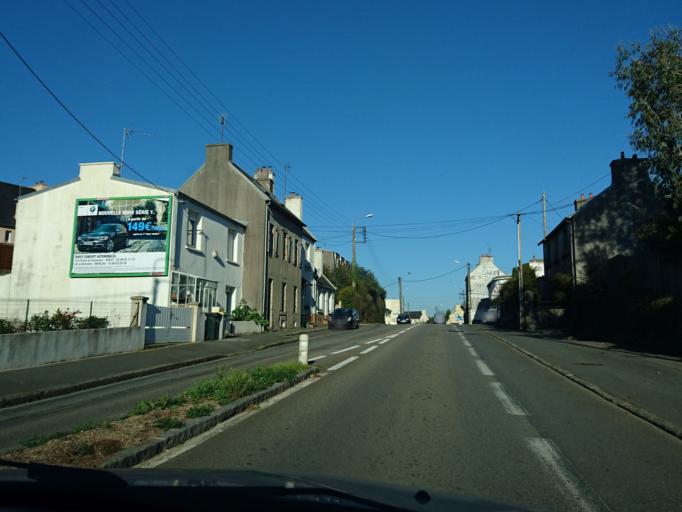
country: FR
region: Brittany
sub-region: Departement du Finistere
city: Brest
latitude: 48.4117
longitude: -4.4531
